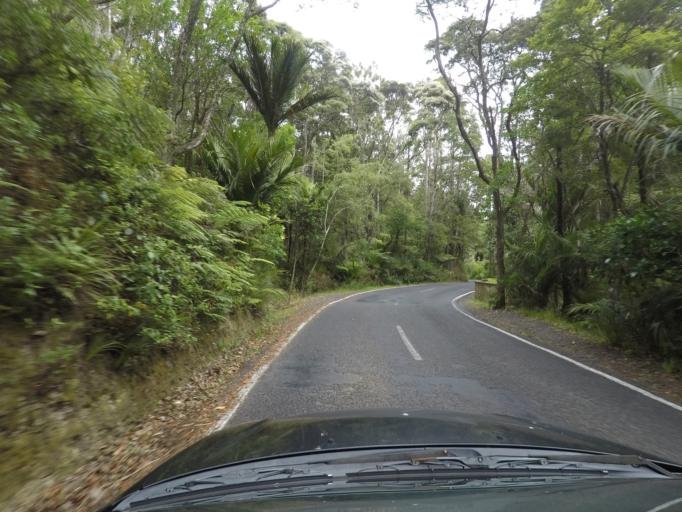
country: NZ
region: Auckland
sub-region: Auckland
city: Titirangi
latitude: -36.9487
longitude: 174.6584
